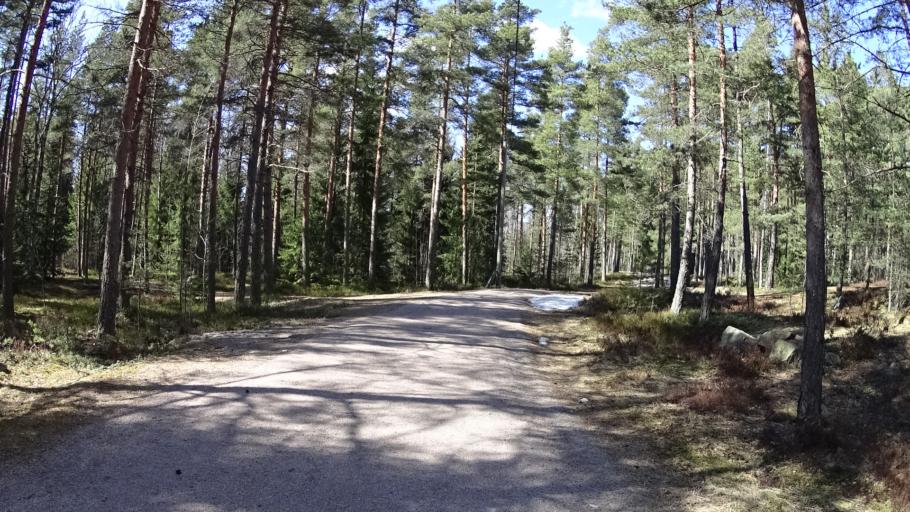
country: FI
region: Uusimaa
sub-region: Helsinki
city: Kilo
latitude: 60.2314
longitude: 24.7894
